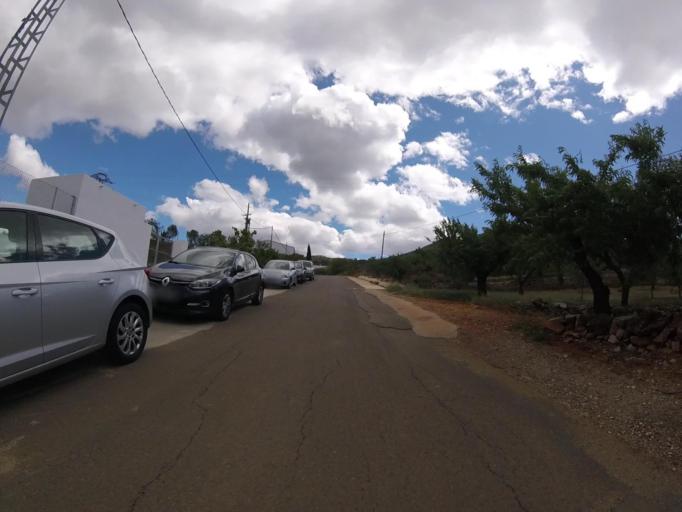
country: ES
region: Valencia
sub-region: Provincia de Castello
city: Sierra-Engarceran
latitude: 40.2919
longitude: -0.0488
